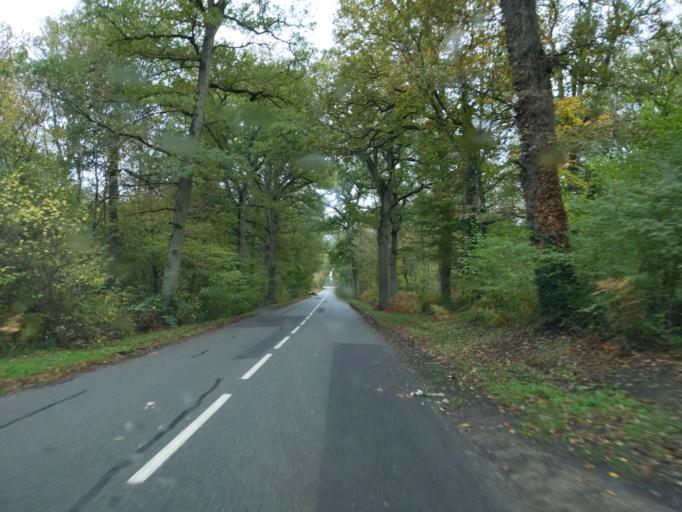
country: FR
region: Ile-de-France
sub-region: Departement des Yvelines
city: Saint-Arnoult-en-Yvelines
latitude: 48.6068
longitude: 1.9495
